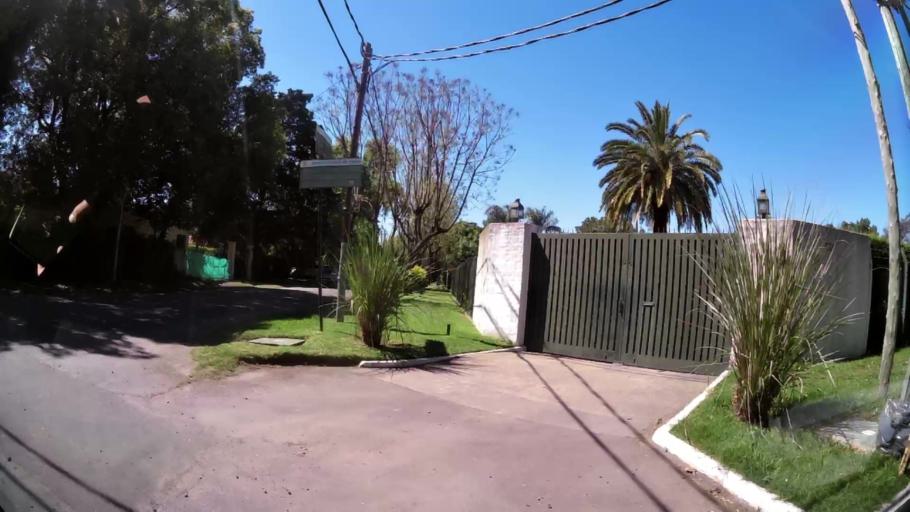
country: AR
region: Buenos Aires
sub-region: Partido de Tigre
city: Tigre
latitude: -34.4960
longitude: -58.6218
